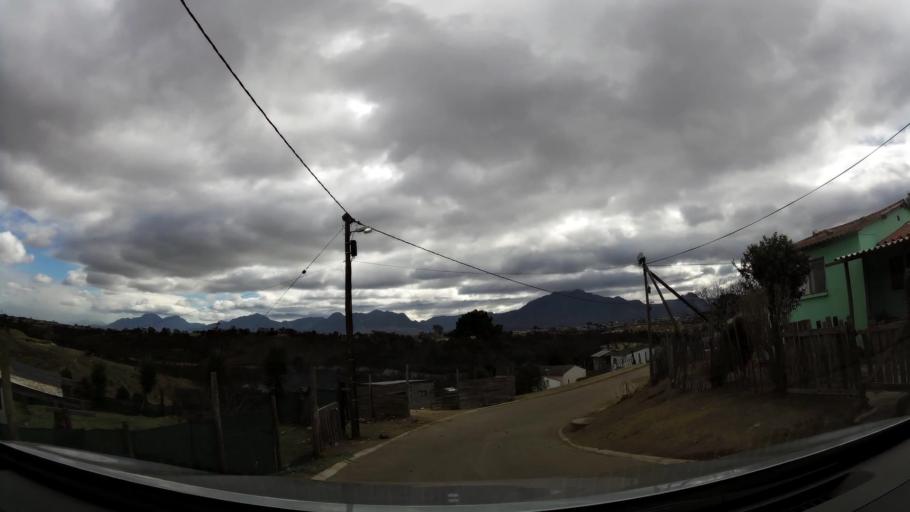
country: ZA
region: Western Cape
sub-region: Eden District Municipality
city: George
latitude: -34.0147
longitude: 22.4760
